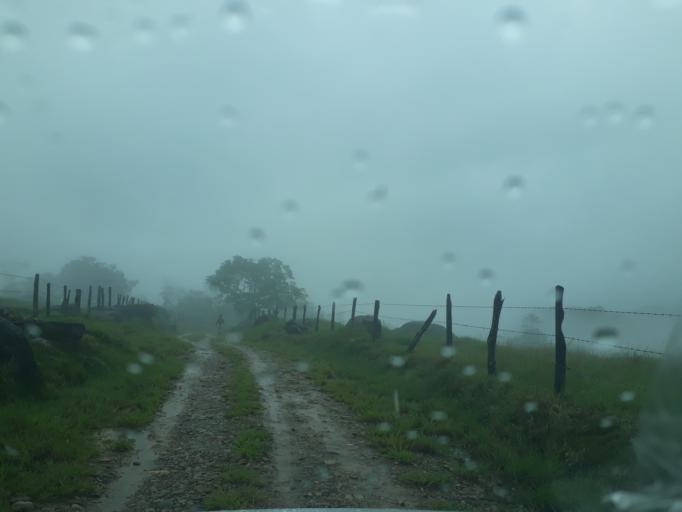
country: CO
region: Cundinamarca
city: Medina
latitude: 4.5315
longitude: -73.3781
